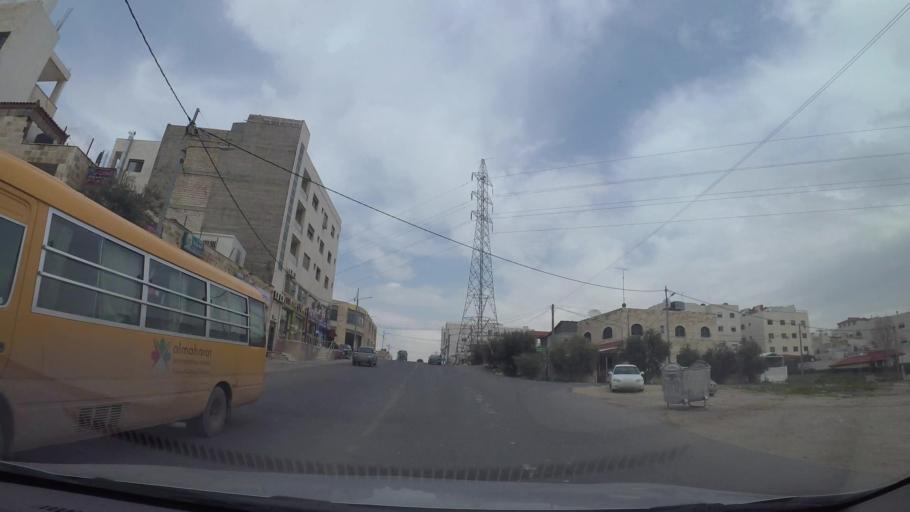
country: JO
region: Amman
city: Umm as Summaq
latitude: 31.8951
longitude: 35.8638
